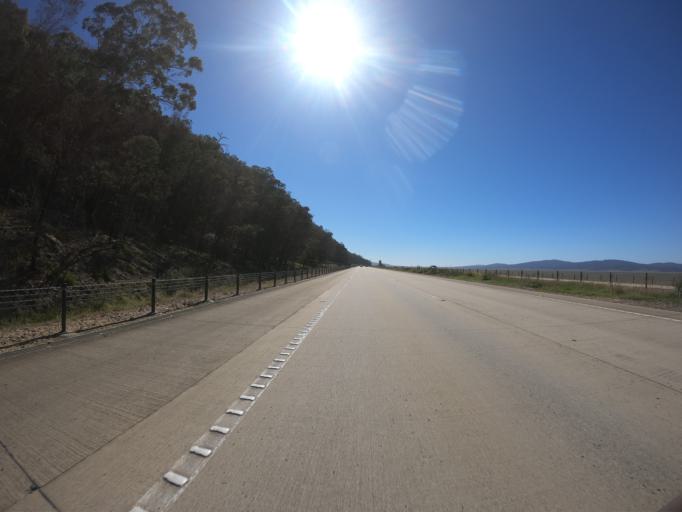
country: AU
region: New South Wales
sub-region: Yass Valley
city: Gundaroo
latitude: -35.0549
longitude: 149.3750
